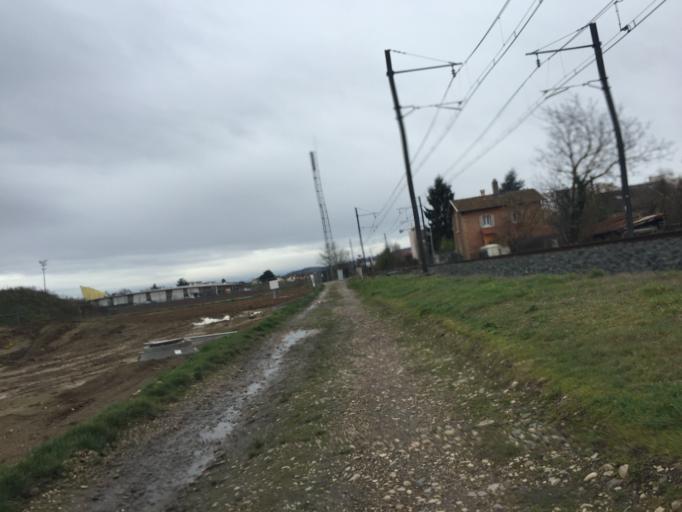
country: FR
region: Rhone-Alpes
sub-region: Departement de l'Ain
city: Saint-Maurice-de-Beynost
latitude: 45.8298
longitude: 4.9885
